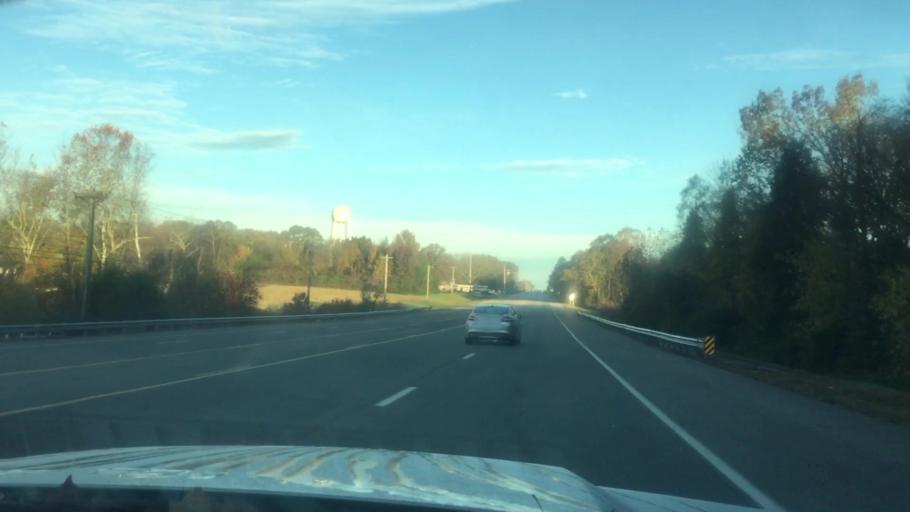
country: US
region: Tennessee
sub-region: Coffee County
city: Tullahoma
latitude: 35.3301
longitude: -86.1808
